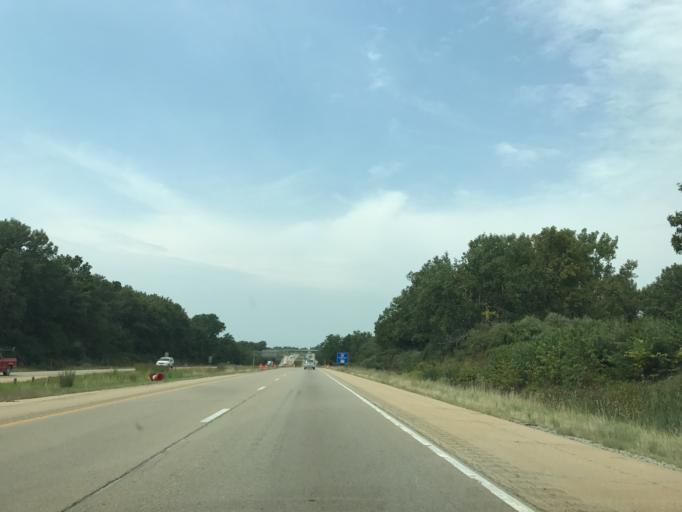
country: US
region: Illinois
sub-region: LaSalle County
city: La Salle
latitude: 41.3719
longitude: -89.0827
